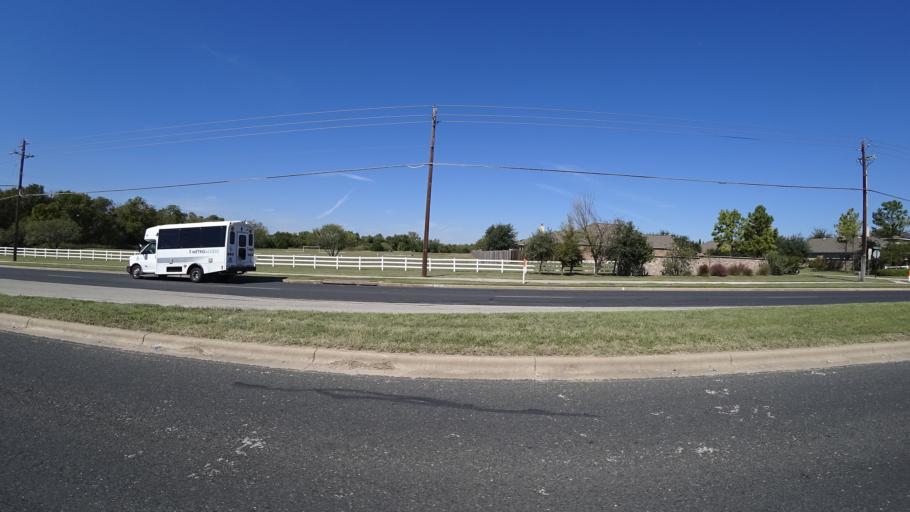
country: US
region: Texas
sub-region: Travis County
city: Austin
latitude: 30.1942
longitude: -97.6957
